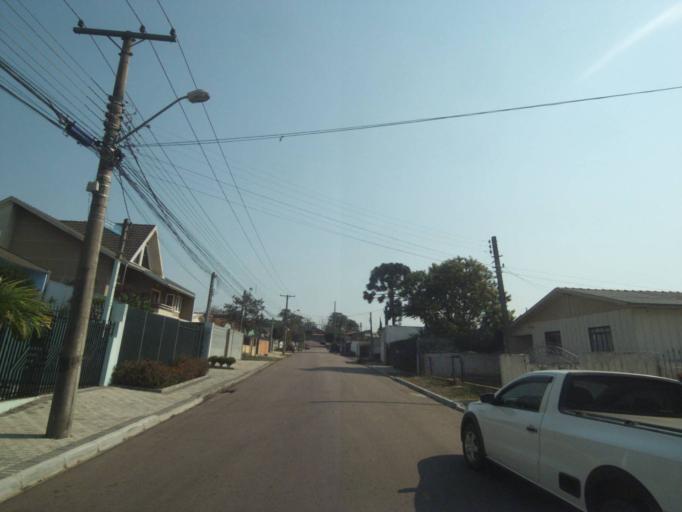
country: BR
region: Parana
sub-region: Sao Jose Dos Pinhais
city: Sao Jose dos Pinhais
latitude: -25.5122
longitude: -49.2812
